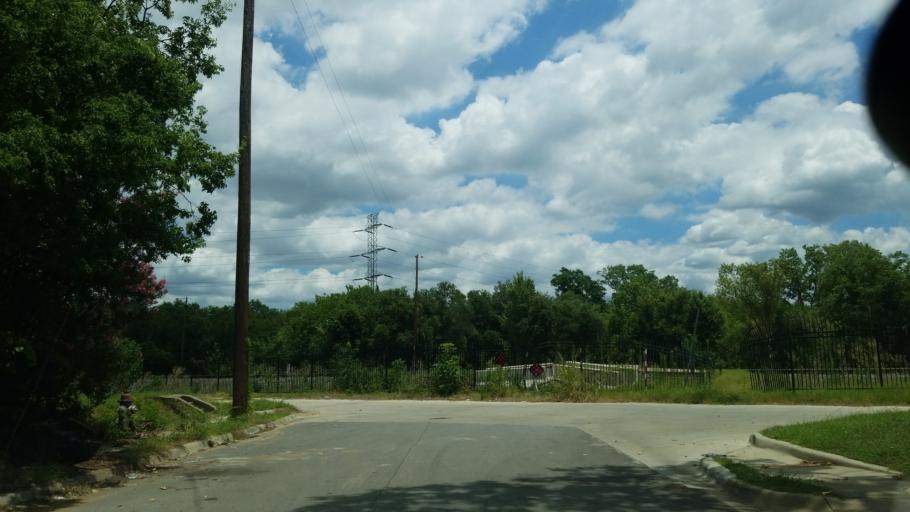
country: US
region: Texas
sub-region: Dallas County
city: Dallas
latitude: 32.7507
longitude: -96.7480
